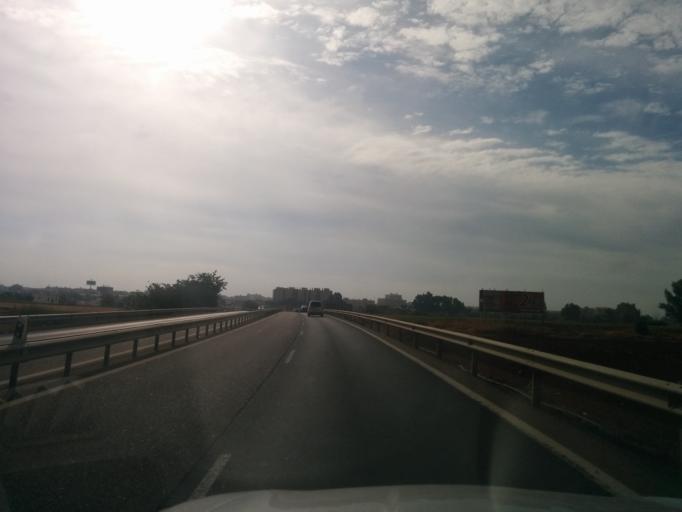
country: ES
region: Andalusia
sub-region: Provincia de Sevilla
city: Sevilla
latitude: 37.4156
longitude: -5.9426
